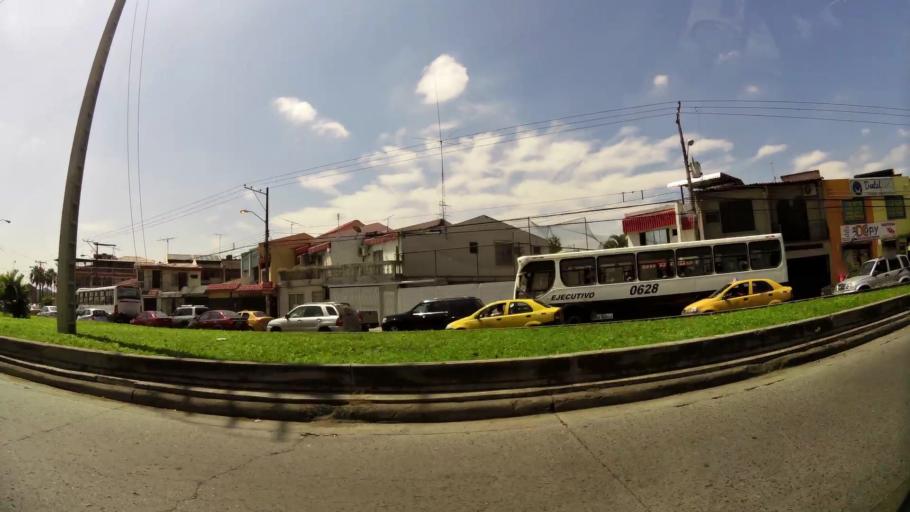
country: EC
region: Guayas
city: Eloy Alfaro
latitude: -2.1409
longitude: -79.9087
